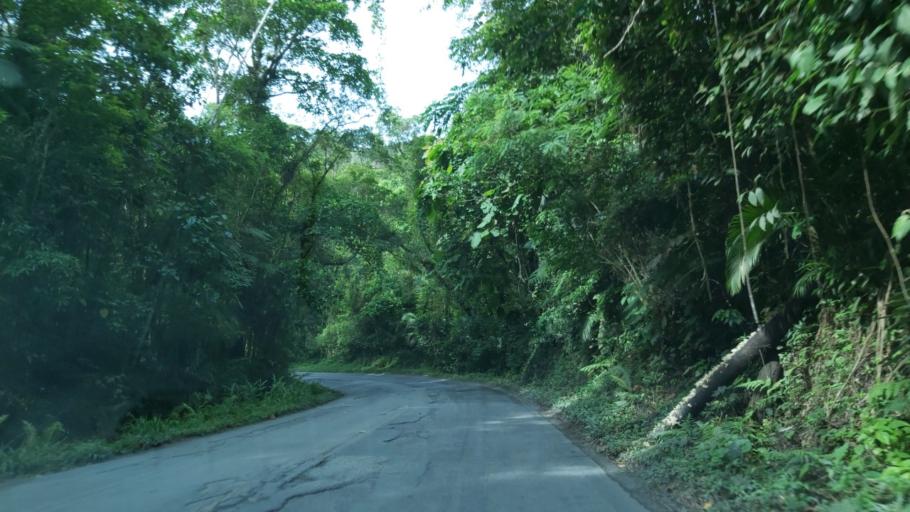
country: BR
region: Sao Paulo
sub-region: Miracatu
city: Miracatu
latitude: -24.0566
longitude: -47.5776
